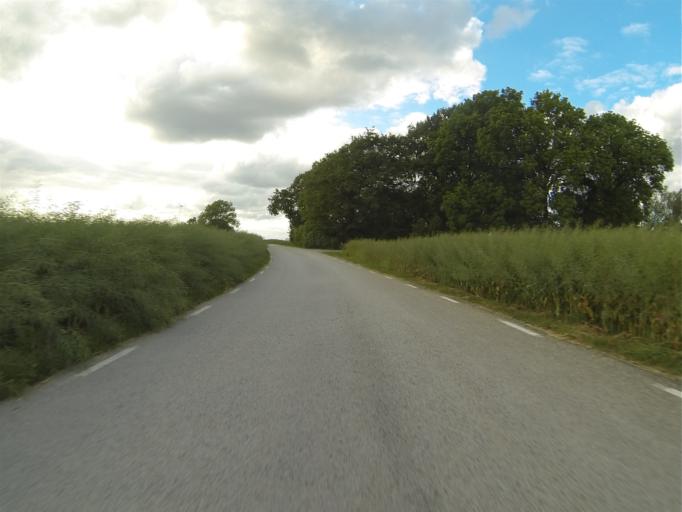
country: SE
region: Skane
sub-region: Staffanstorps Kommun
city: Staffanstorp
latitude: 55.6690
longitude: 13.2455
